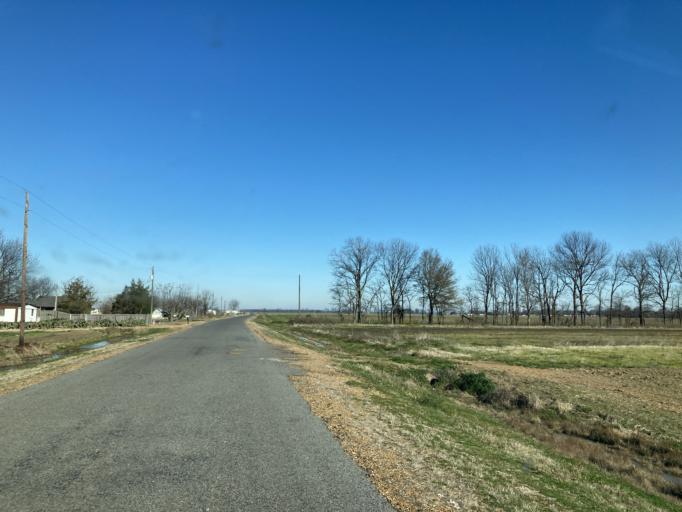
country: US
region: Mississippi
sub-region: Yazoo County
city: Yazoo City
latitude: 32.9626
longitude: -90.6056
